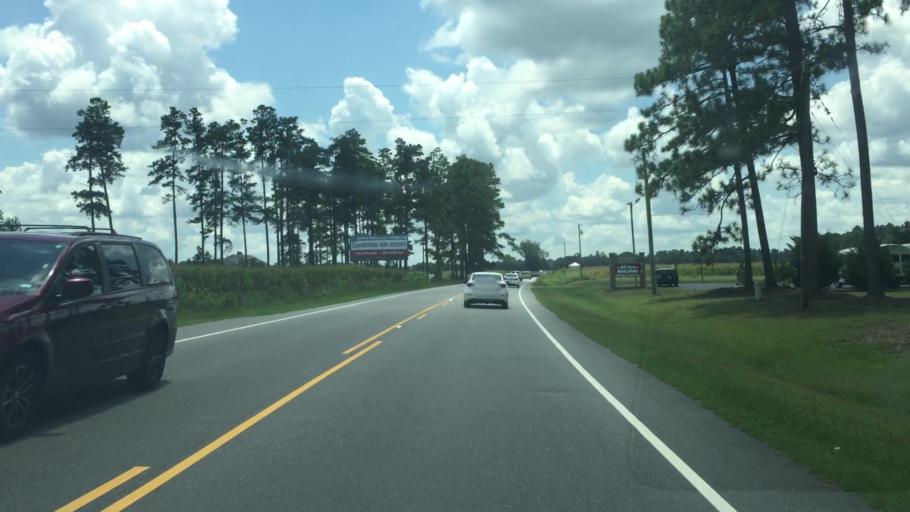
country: US
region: North Carolina
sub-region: Columbus County
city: Tabor City
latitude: 34.1765
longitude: -78.8403
